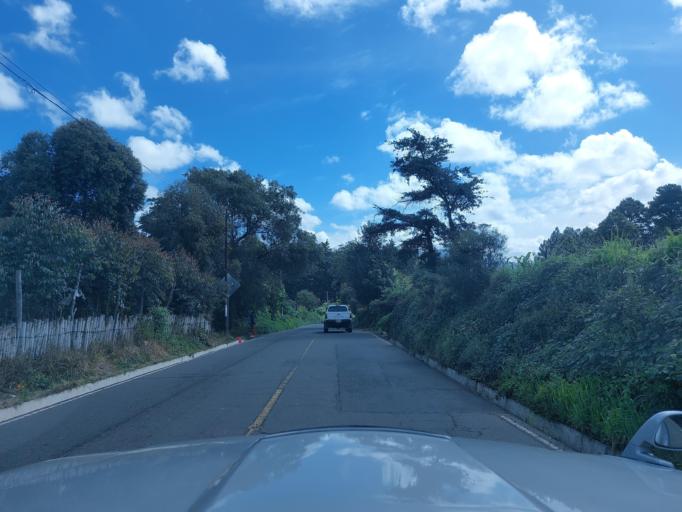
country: GT
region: Chimaltenango
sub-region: Municipio de Santa Cruz Balanya
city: Santa Cruz Balanya
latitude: 14.6781
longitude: -90.8971
